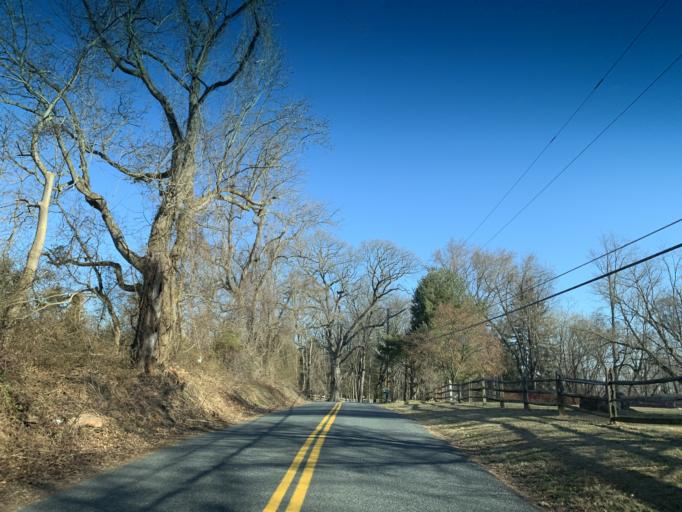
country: US
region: Maryland
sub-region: Harford County
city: Aberdeen
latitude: 39.6059
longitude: -76.2239
